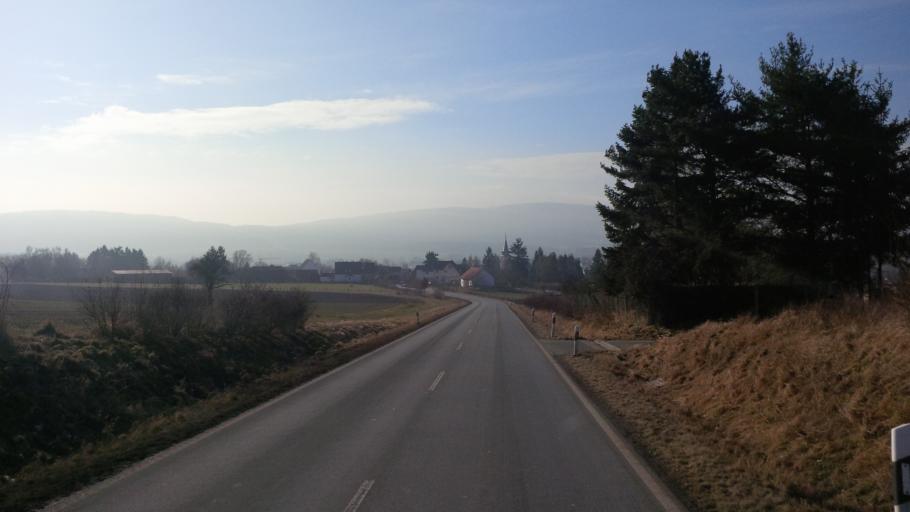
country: DE
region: Hesse
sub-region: Regierungsbezirk Darmstadt
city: Wehrheim
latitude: 50.3094
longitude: 8.5757
